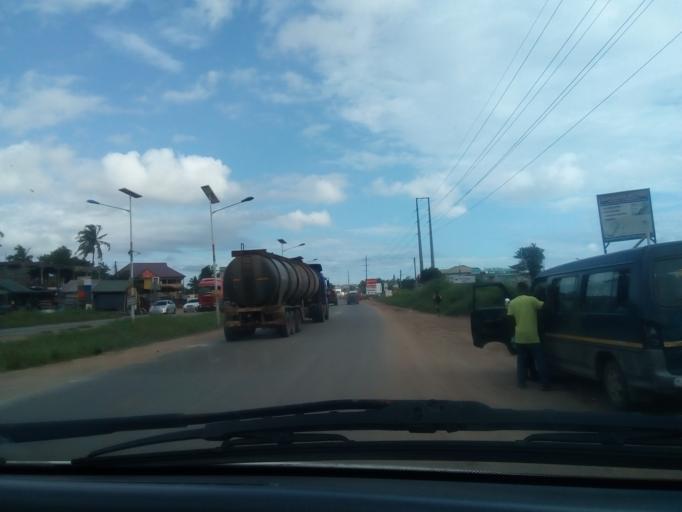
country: GH
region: Greater Accra
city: Achiaman
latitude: 5.7034
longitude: -0.2969
